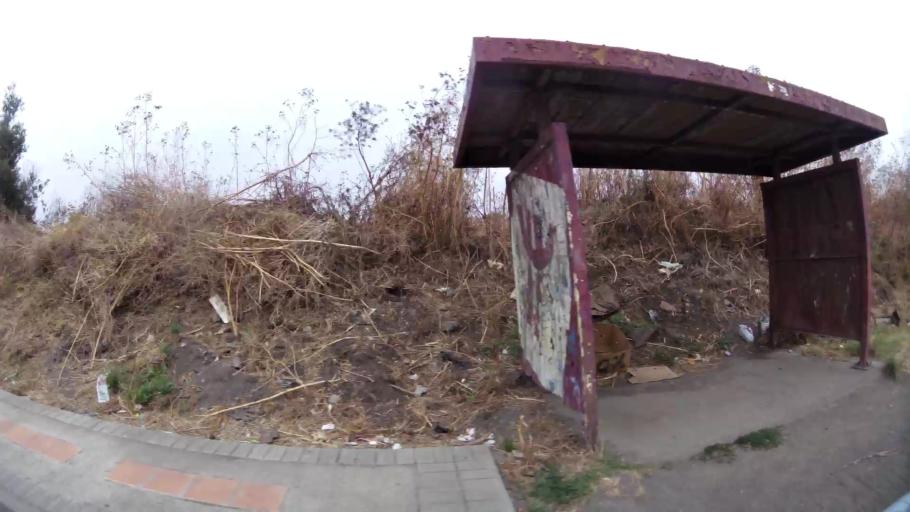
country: CL
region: Biobio
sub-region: Provincia de Concepcion
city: Concepcion
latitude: -36.7974
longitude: -73.0830
